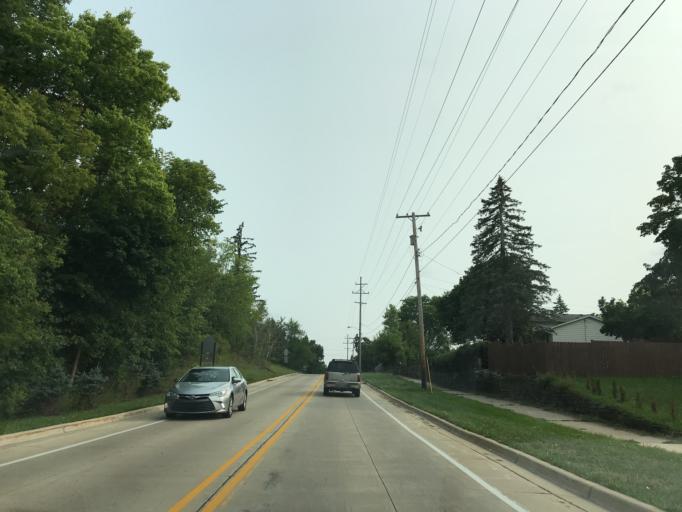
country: US
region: Michigan
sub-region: Ingham County
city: Okemos
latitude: 42.7401
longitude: -84.4475
